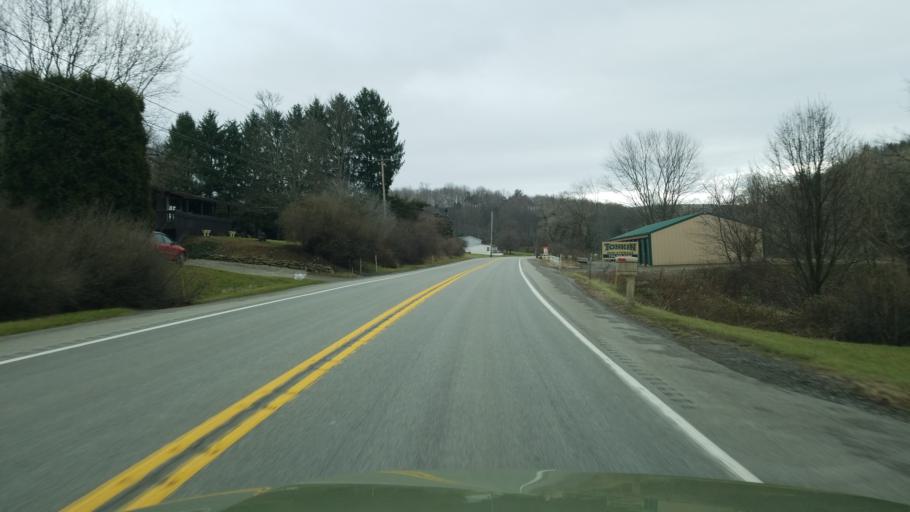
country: US
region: Pennsylvania
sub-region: Indiana County
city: Chevy Chase Heights
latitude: 40.7169
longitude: -79.1025
